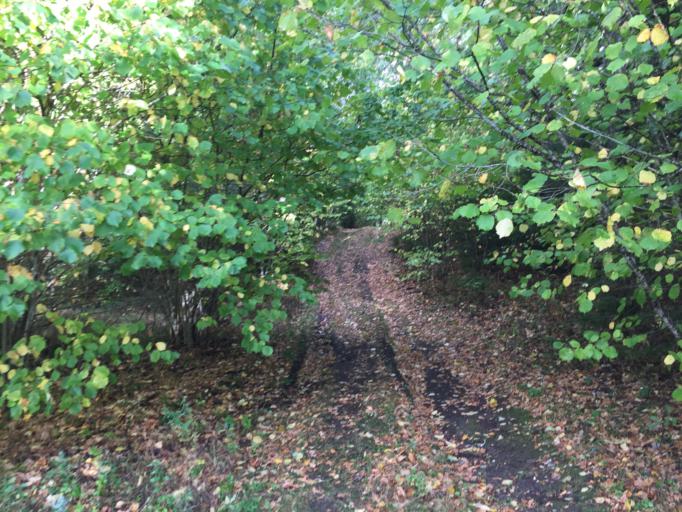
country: LV
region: Ligatne
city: Ligatne
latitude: 57.1149
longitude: 25.1370
